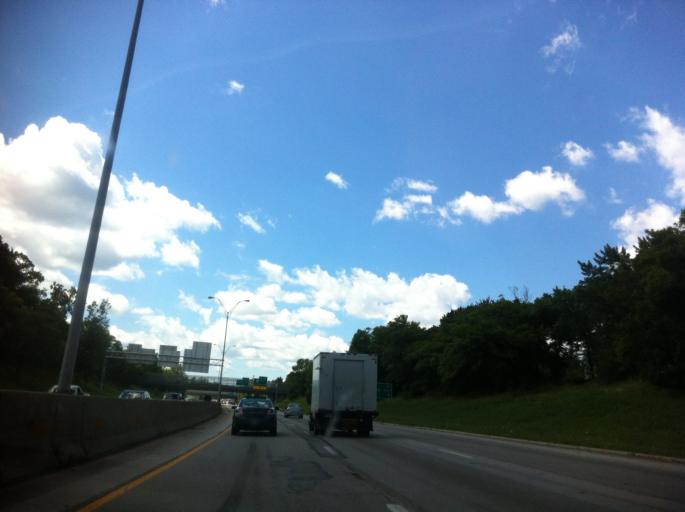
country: US
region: Ohio
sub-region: Lucas County
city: Ottawa Hills
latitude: 41.6858
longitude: -83.6073
